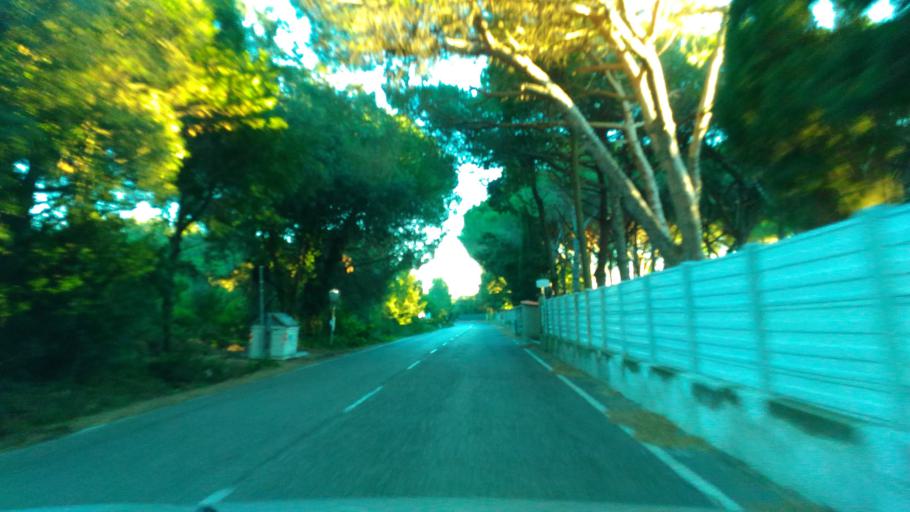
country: IT
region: Tuscany
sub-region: Provincia di Livorno
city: Quercianella
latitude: 43.4329
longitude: 10.3904
